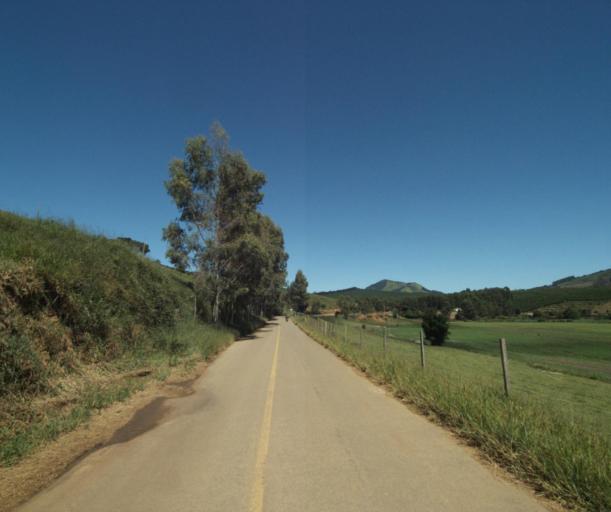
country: BR
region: Minas Gerais
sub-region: Espera Feliz
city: Espera Feliz
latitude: -20.5766
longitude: -41.8322
